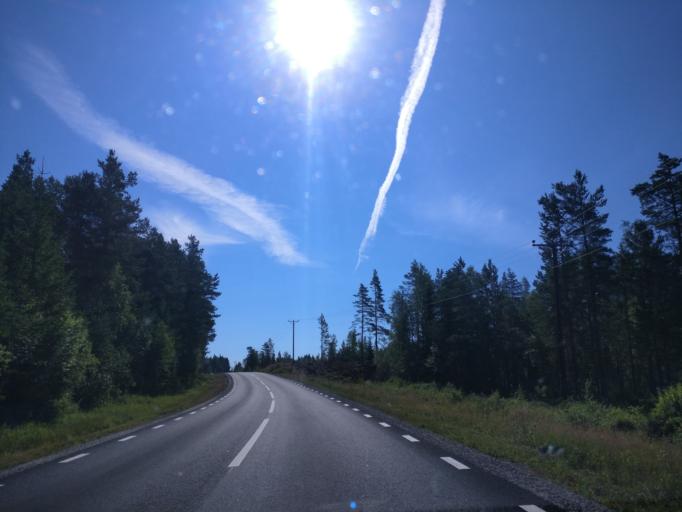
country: SE
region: Vaermland
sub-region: Hagfors Kommun
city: Hagfors
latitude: 60.0315
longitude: 13.8514
